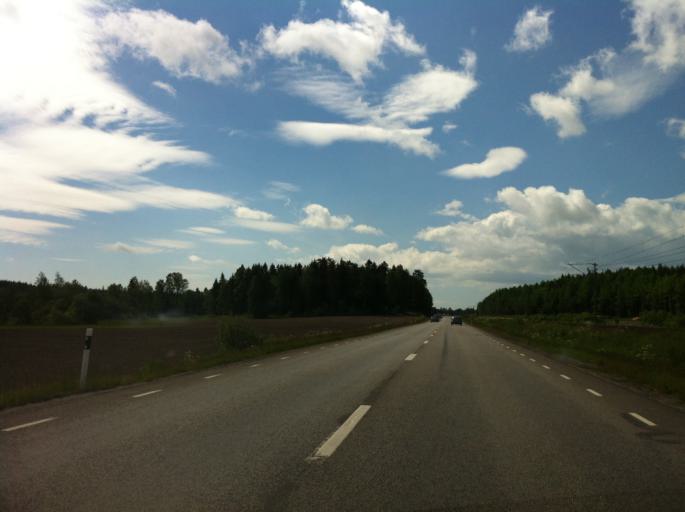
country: SE
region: Vaermland
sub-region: Saffle Kommun
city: Saeffle
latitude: 59.1748
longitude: 13.0052
